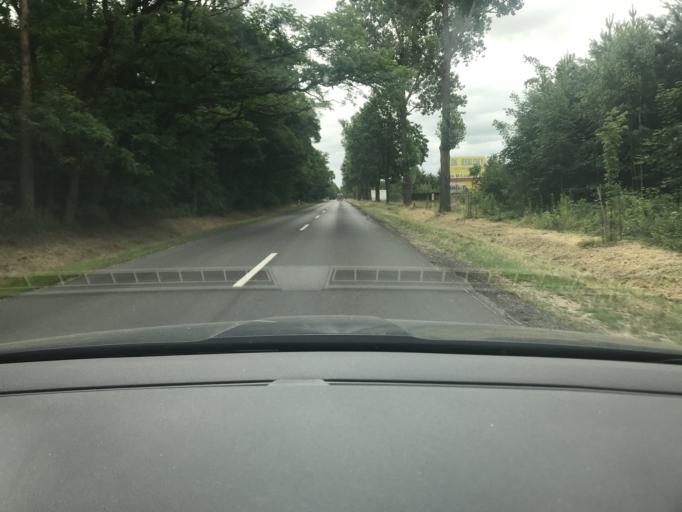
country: PL
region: Lodz Voivodeship
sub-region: Powiat poddebicki
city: Poddebice
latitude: 51.8874
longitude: 18.9930
